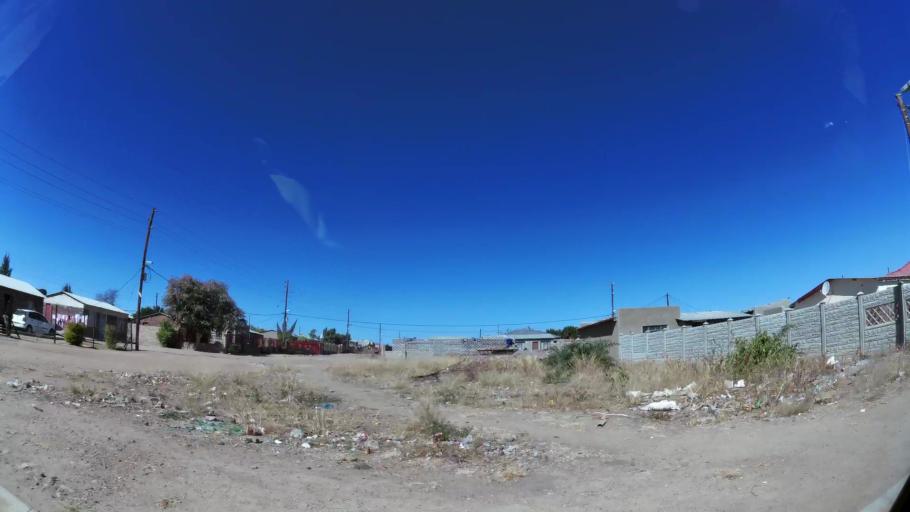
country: ZA
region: Limpopo
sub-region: Capricorn District Municipality
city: Polokwane
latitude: -23.8480
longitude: 29.4118
